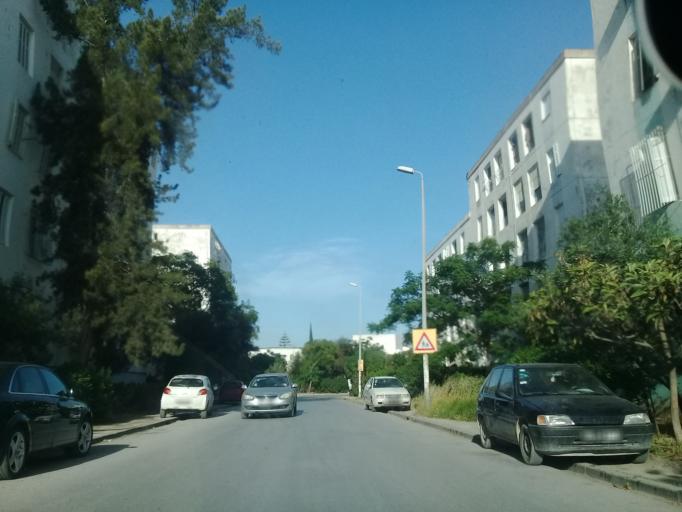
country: TN
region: Ariana
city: Ariana
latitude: 36.8384
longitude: 10.1951
